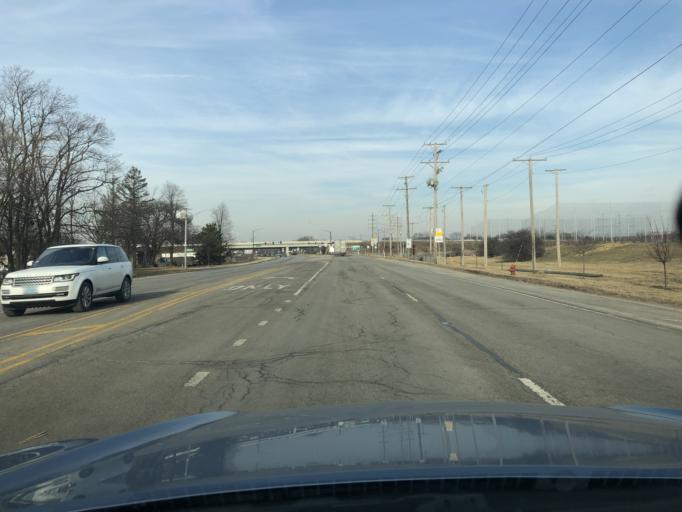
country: US
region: Illinois
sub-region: DuPage County
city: Itasca
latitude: 41.9799
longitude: -87.9981
